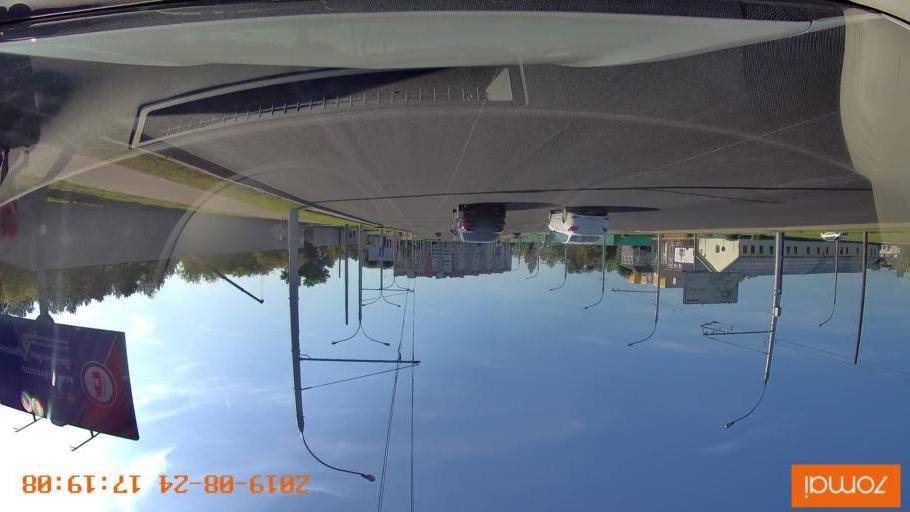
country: BY
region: Minsk
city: Vyaliki Trastsyanets
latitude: 53.8642
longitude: 27.6429
